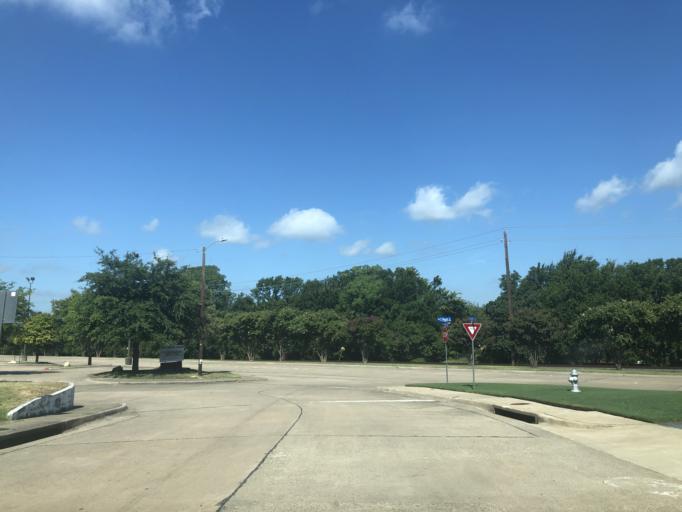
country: US
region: Texas
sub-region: Dallas County
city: Duncanville
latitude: 32.6479
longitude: -96.9124
